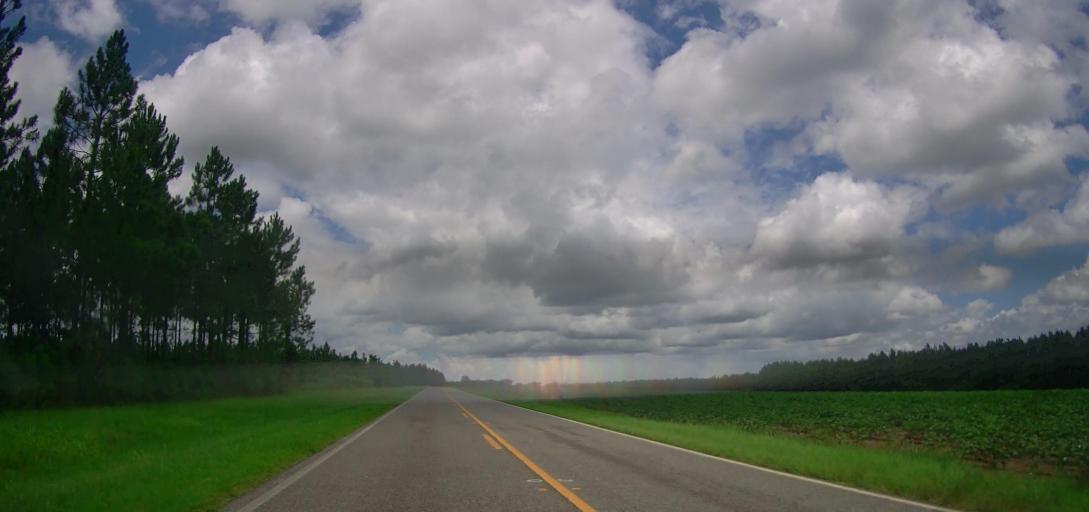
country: US
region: Georgia
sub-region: Wilcox County
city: Rochelle
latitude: 31.8720
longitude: -83.5584
